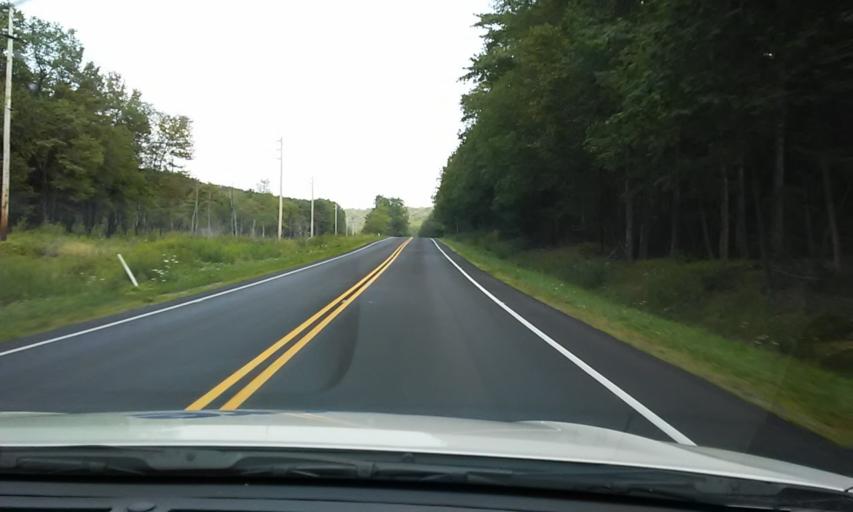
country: US
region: Pennsylvania
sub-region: Elk County
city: Saint Marys
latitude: 41.4526
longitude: -78.4378
